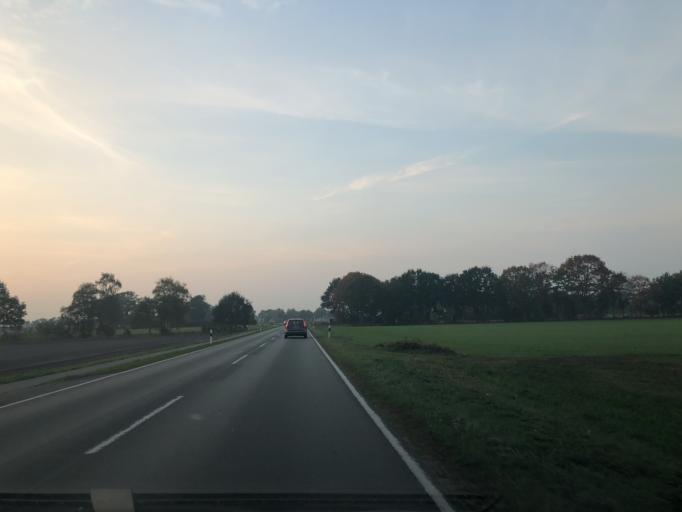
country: DE
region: Lower Saxony
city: Bosel
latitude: 53.0135
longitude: 7.9093
